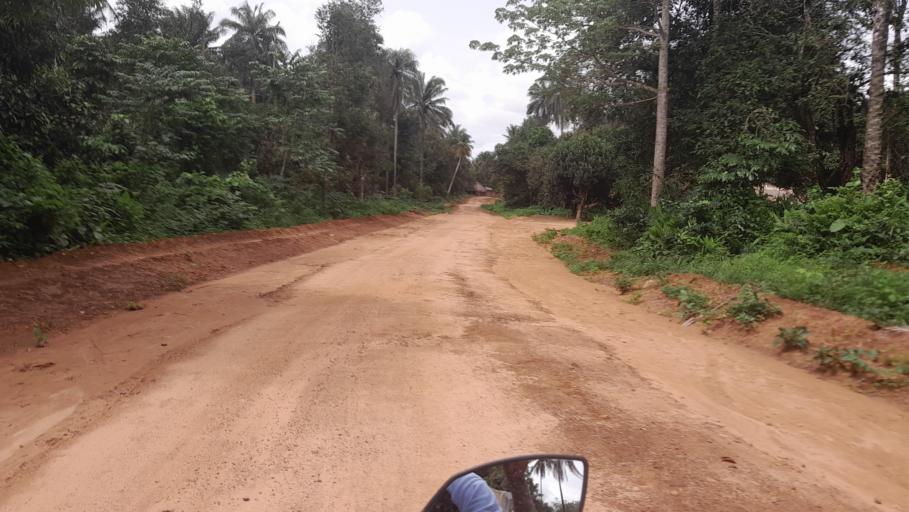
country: GN
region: Boke
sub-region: Boffa
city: Boffa
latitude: 10.0843
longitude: -13.8646
